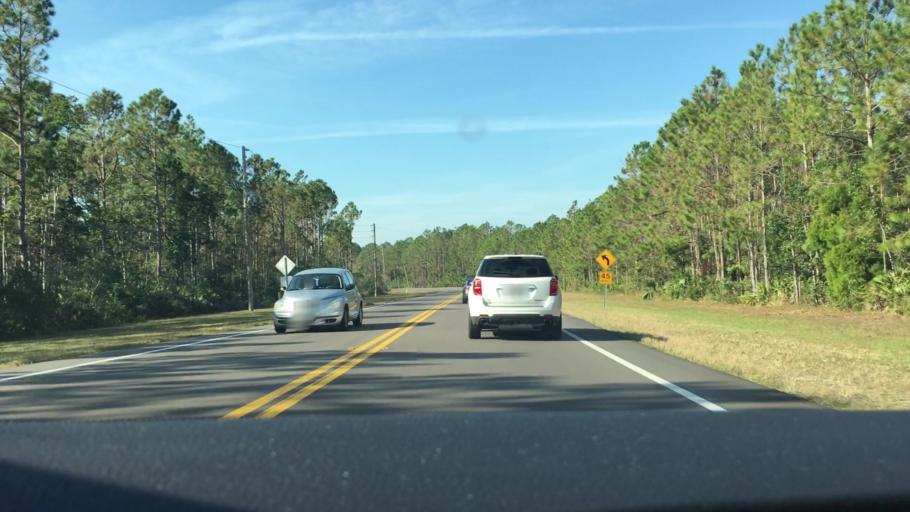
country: US
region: Florida
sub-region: Volusia County
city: Ormond Beach
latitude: 29.2517
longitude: -81.1047
